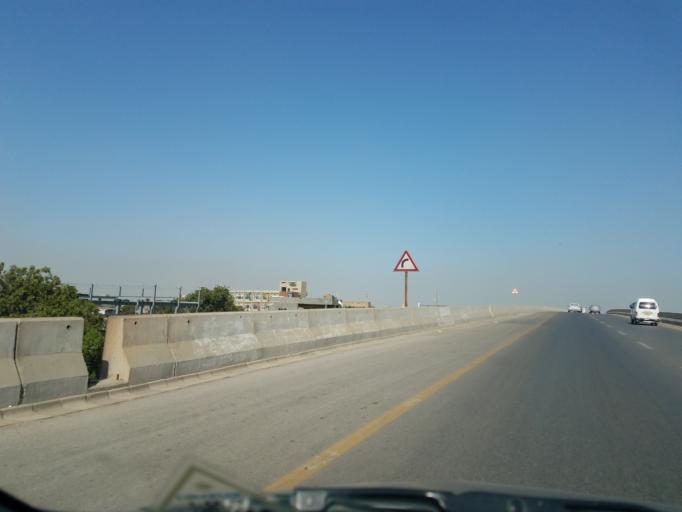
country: PK
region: Sindh
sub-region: Karachi District
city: Karachi
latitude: 24.8809
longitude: 66.9925
